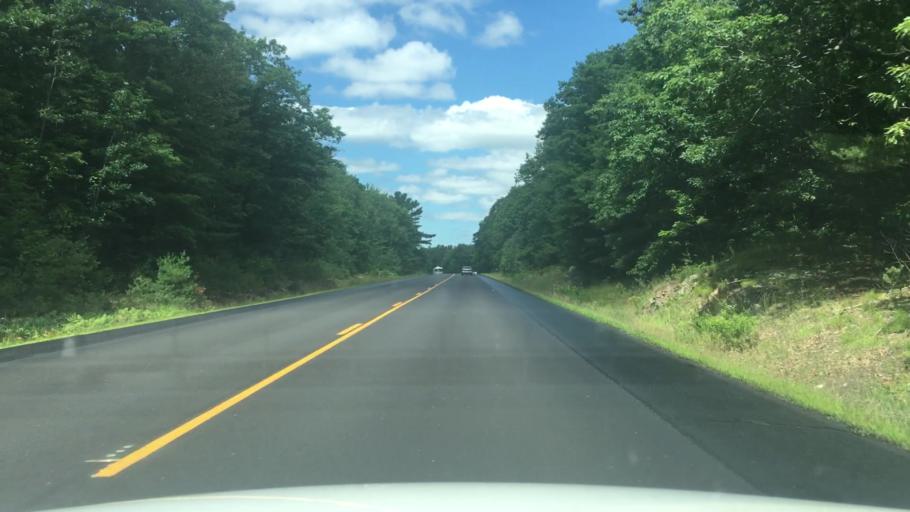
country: US
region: Maine
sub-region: Waldo County
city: Searsmont
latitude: 44.4070
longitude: -69.1717
